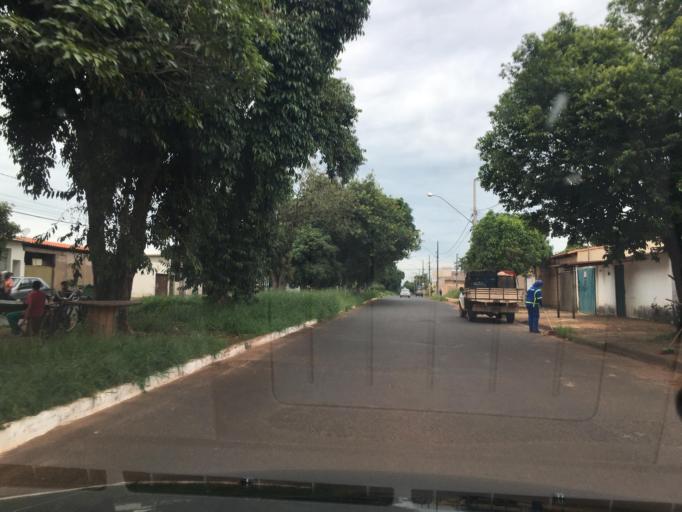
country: BR
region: Minas Gerais
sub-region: Uberlandia
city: Uberlandia
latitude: -18.8748
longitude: -48.2262
